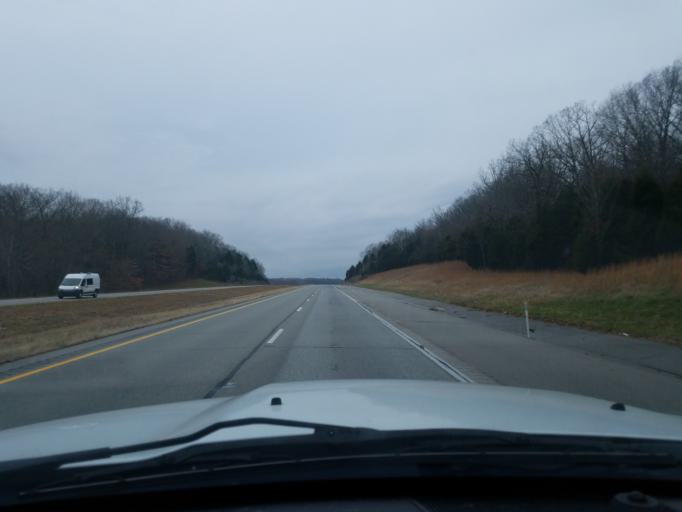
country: US
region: Indiana
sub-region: Crawford County
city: English
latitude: 38.2530
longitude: -86.3175
